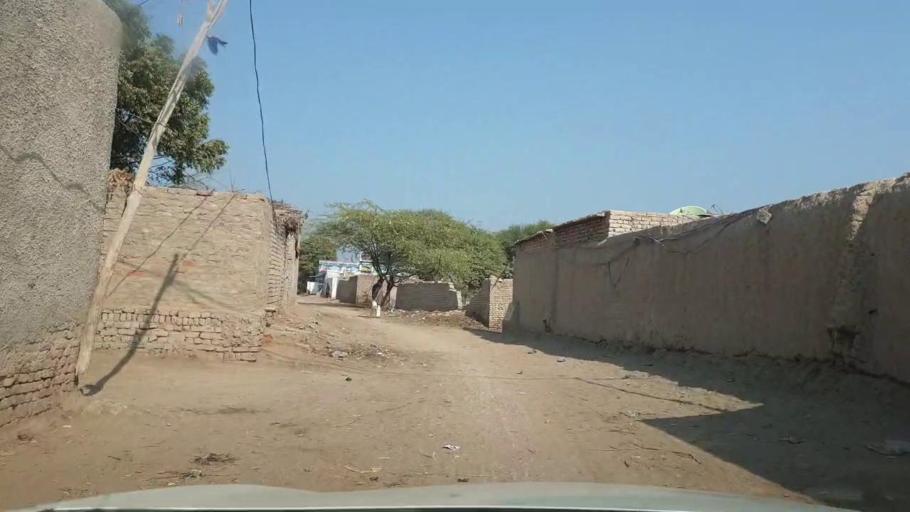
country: PK
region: Sindh
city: Bhit Shah
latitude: 25.7474
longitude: 68.4791
